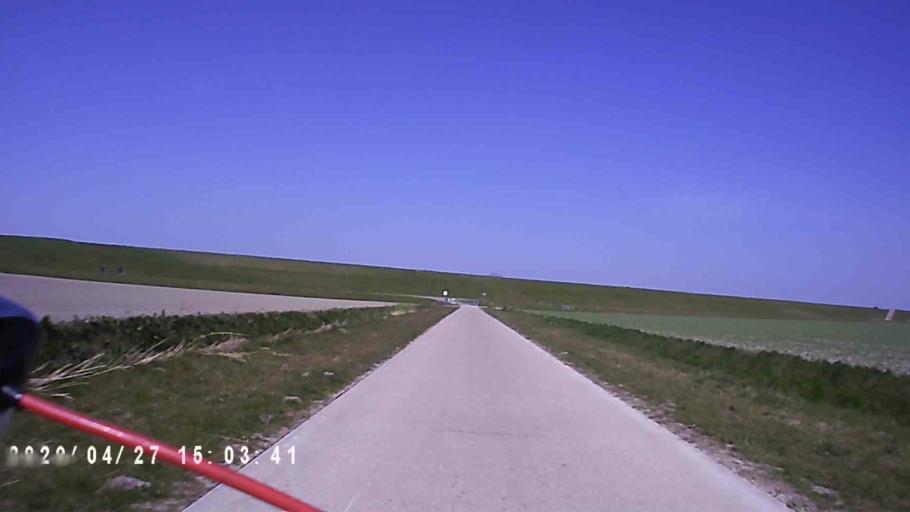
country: NL
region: Groningen
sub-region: Gemeente Winsum
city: Winsum
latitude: 53.4208
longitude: 6.4610
